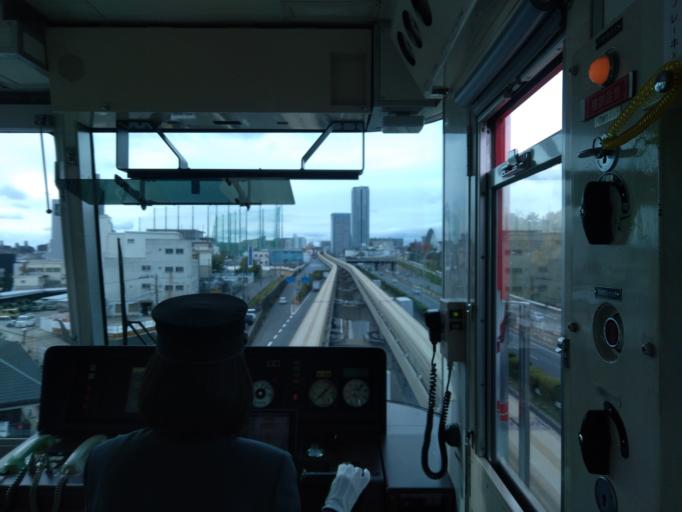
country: JP
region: Osaka
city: Mino
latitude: 34.8065
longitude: 135.5078
